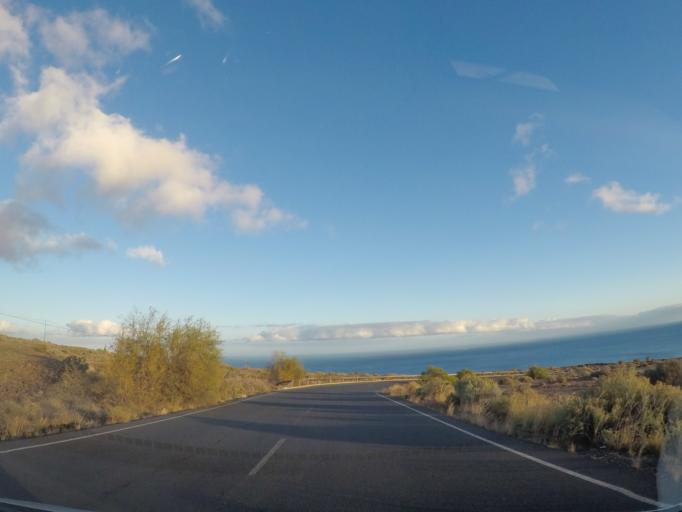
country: ES
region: Canary Islands
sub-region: Provincia de Santa Cruz de Tenerife
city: Alajero
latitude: 28.0369
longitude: -17.2200
